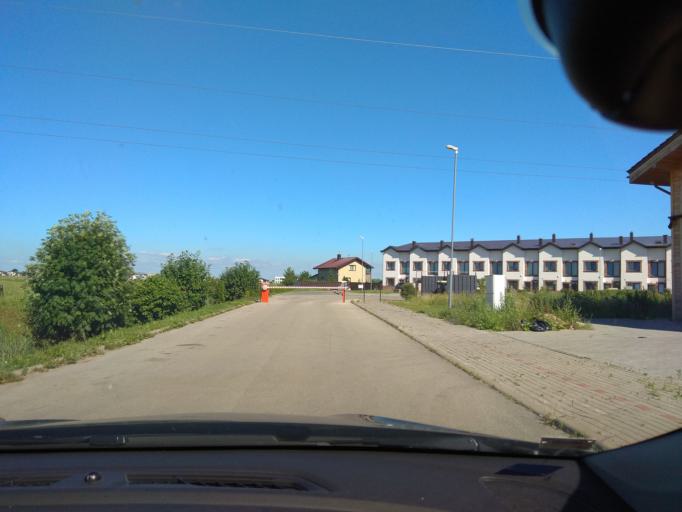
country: LT
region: Klaipedos apskritis
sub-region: Klaipeda
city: Klaipeda
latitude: 55.7490
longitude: 21.1817
